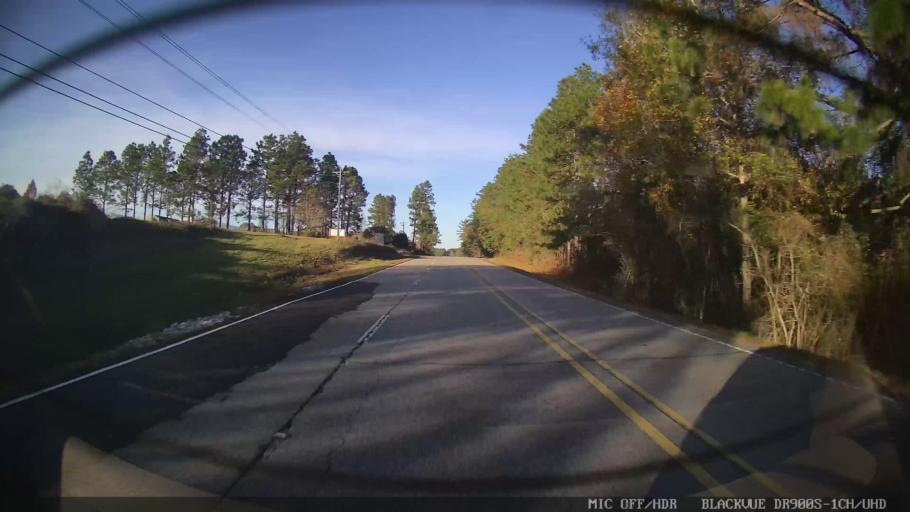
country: US
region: Mississippi
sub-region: Lamar County
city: Purvis
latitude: 31.1041
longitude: -89.4124
